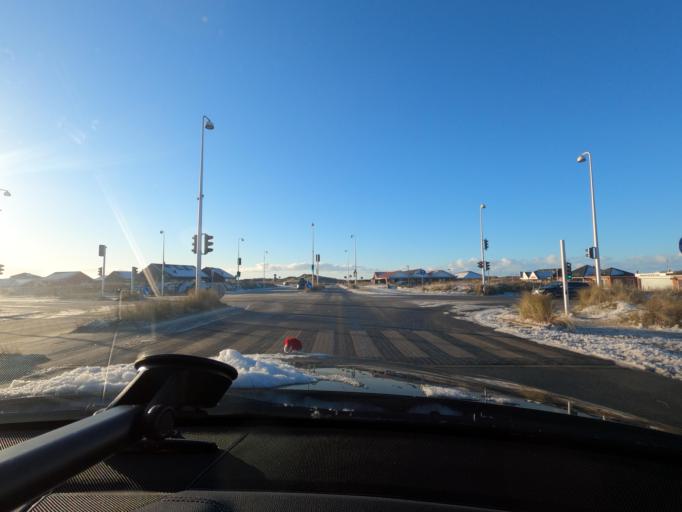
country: DE
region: Schleswig-Holstein
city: List
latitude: 55.1454
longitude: 8.4952
